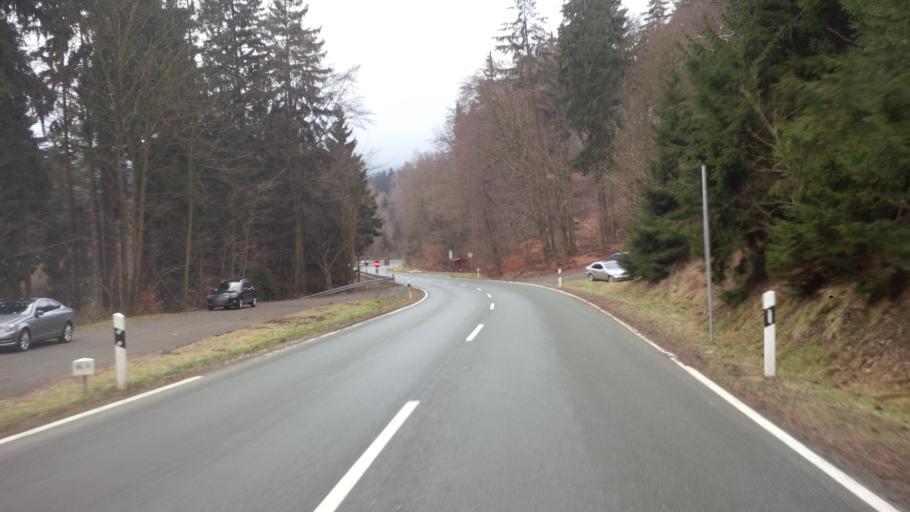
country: DE
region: Hesse
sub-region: Regierungsbezirk Darmstadt
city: Schmitten
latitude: 50.2280
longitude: 8.4804
